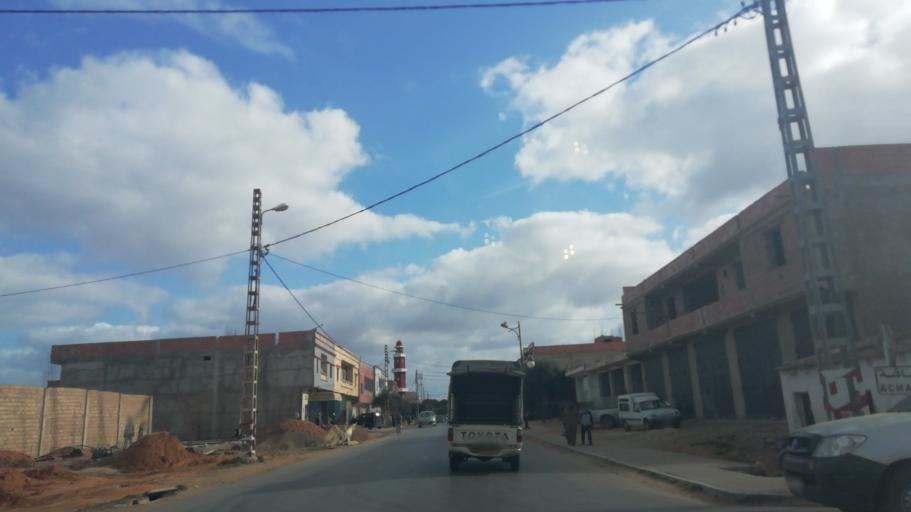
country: DZ
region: Relizane
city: Mazouna
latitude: 36.2683
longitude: 0.6281
